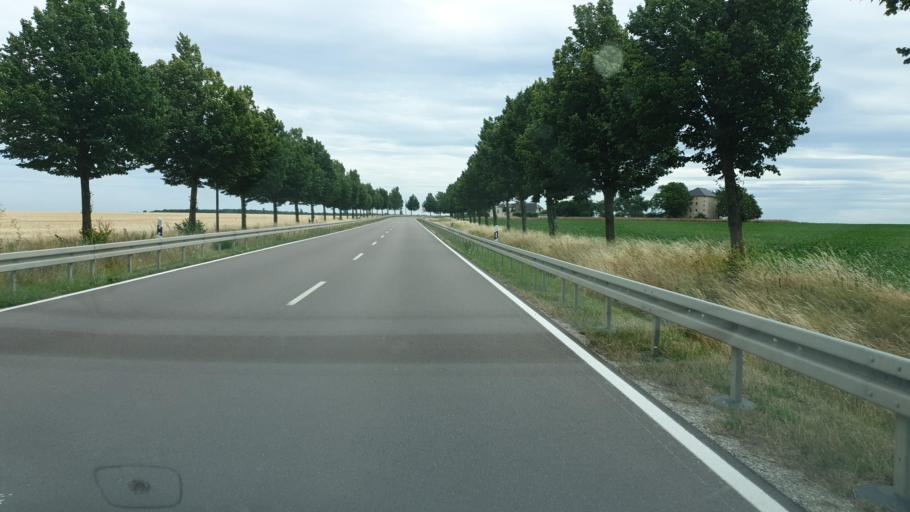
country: DE
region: Saxony-Anhalt
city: Gleina
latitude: 51.2544
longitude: 11.7283
